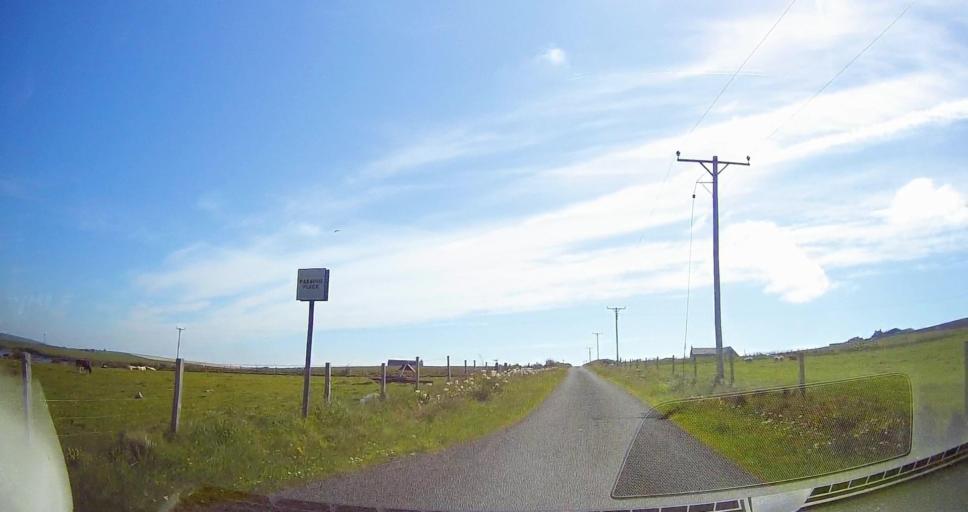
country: GB
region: Scotland
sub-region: Orkney Islands
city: Orkney
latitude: 58.8577
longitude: -2.9386
